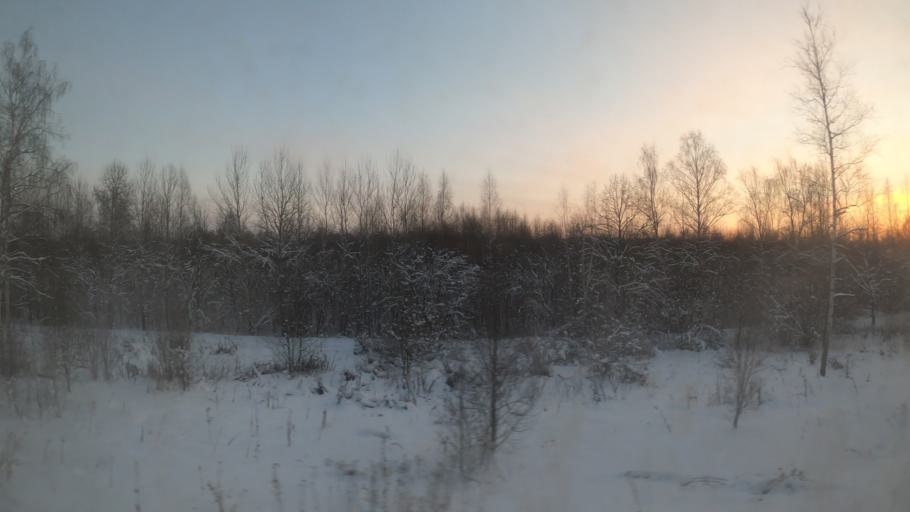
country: RU
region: Moskovskaya
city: Yermolino
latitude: 56.1566
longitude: 37.5011
